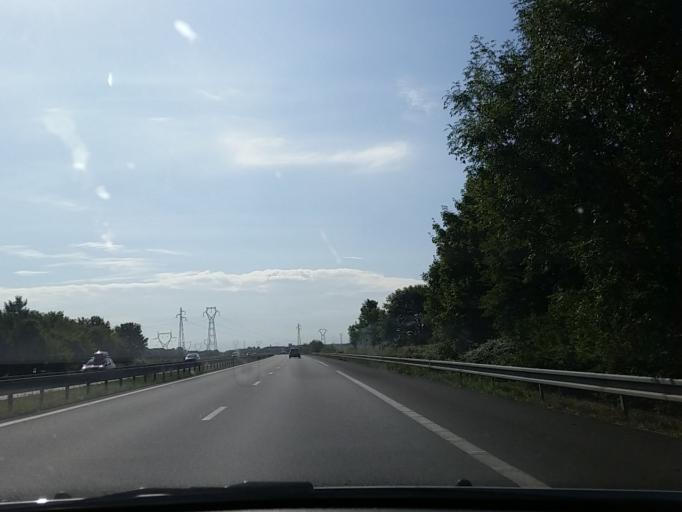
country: FR
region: Centre
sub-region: Departement du Cher
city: Marmagne
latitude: 47.0720
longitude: 2.2805
